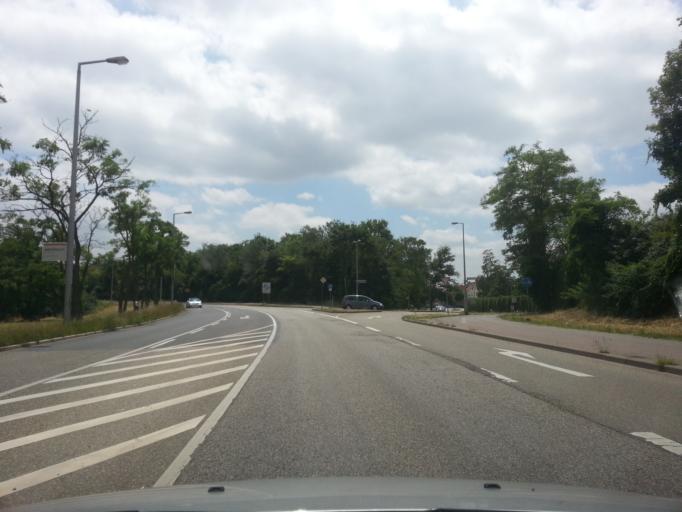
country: DE
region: Baden-Wuerttemberg
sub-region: Karlsruhe Region
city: Bruhl
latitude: 49.4208
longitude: 8.5361
